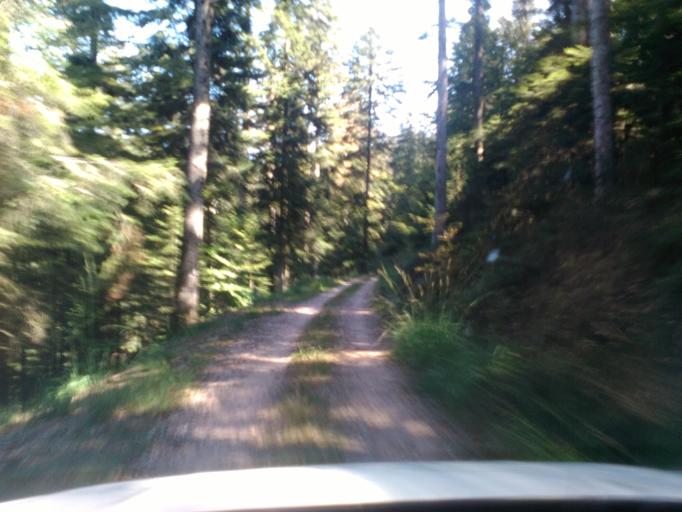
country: FR
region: Lorraine
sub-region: Departement des Vosges
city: Senones
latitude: 48.4331
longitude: 6.9898
